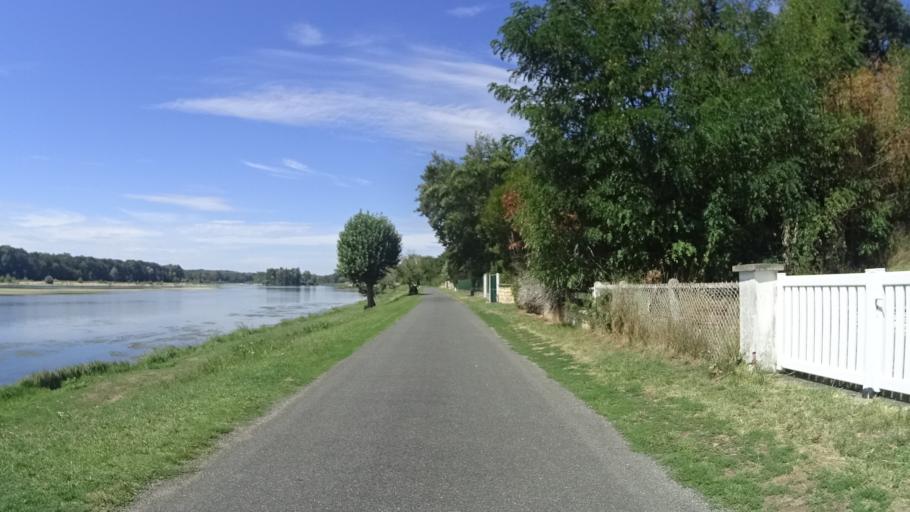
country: FR
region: Centre
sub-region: Departement du Loiret
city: Bonny-sur-Loire
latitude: 47.5850
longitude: 2.7964
